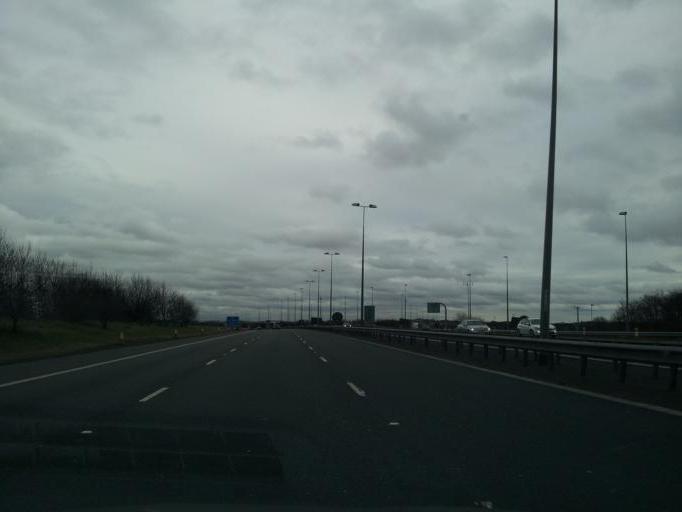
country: GB
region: England
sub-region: Staffordshire
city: Featherstone
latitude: 52.6683
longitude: -2.0714
